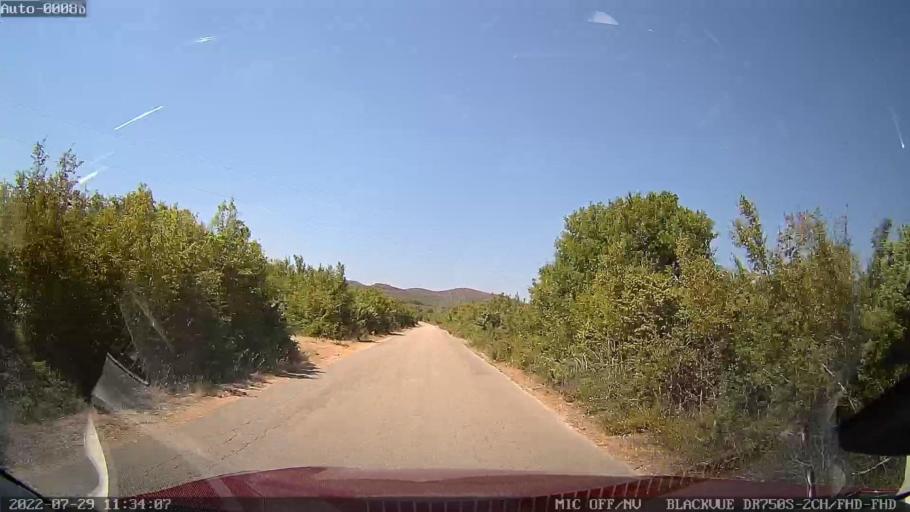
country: HR
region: Zadarska
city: Obrovac
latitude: 44.1809
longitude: 15.7291
